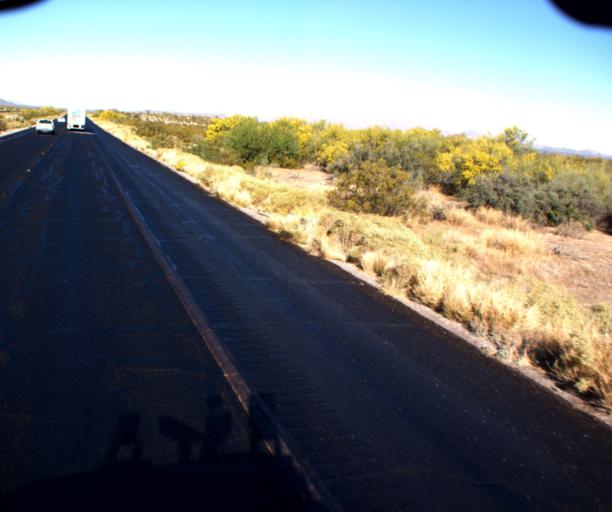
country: US
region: Arizona
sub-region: Pinal County
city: Maricopa
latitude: 32.8366
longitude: -112.2039
